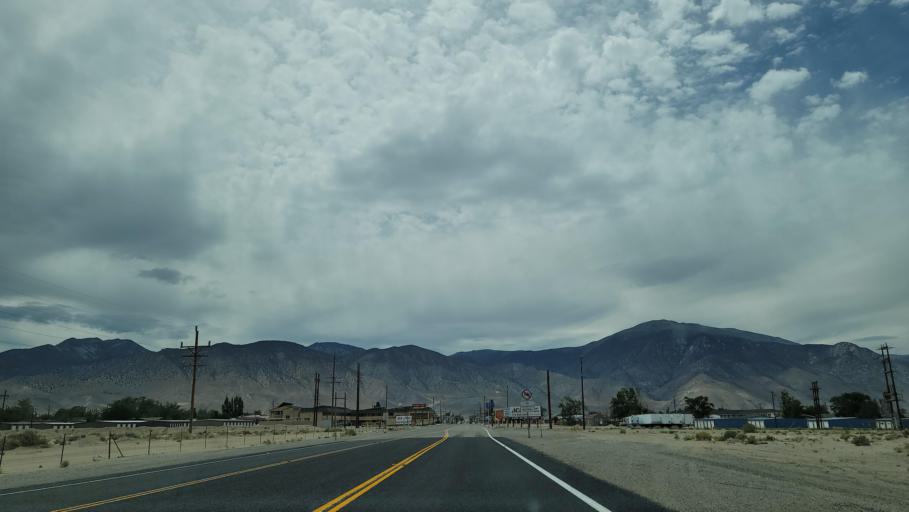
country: US
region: Nevada
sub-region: Mineral County
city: Hawthorne
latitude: 38.5246
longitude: -118.6123
